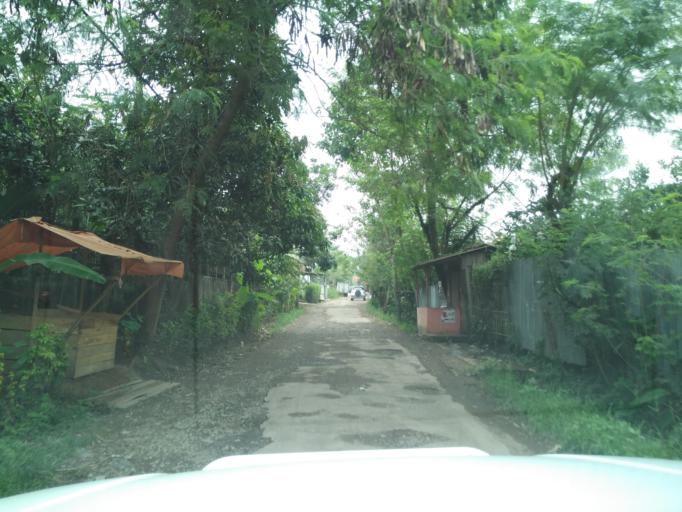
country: ID
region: West Java
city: Ciranjang-hilir
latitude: -6.8122
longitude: 107.1692
